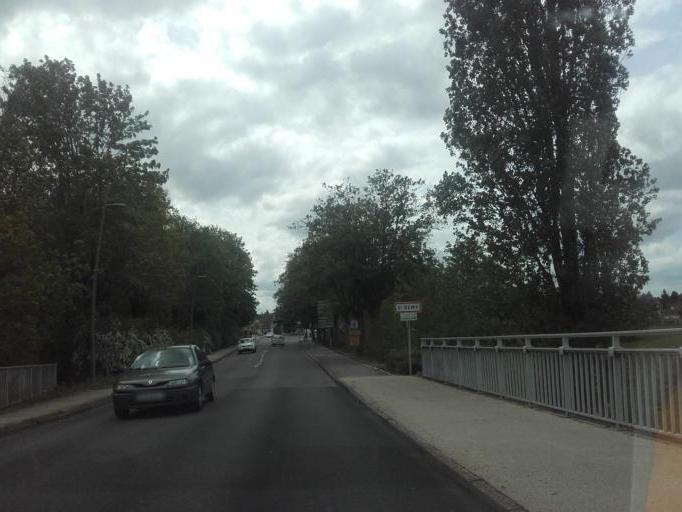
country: FR
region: Bourgogne
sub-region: Departement de Saone-et-Loire
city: Saint-Remy
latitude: 46.7748
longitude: 4.8362
